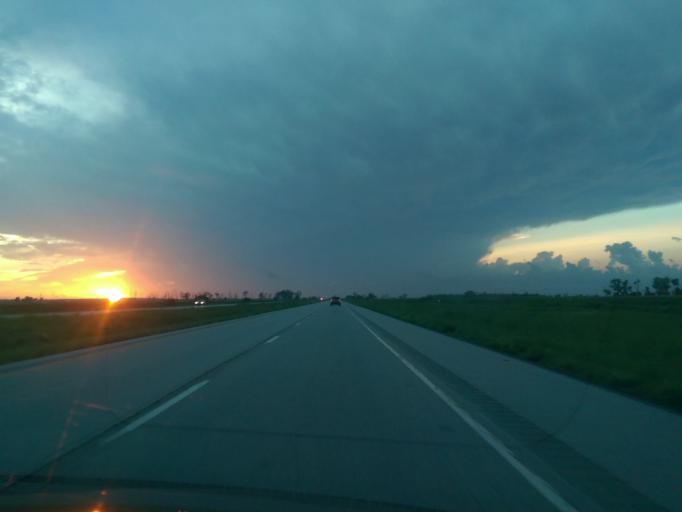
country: US
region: Iowa
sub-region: Fremont County
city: Hamburg
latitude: 40.6125
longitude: -95.6909
